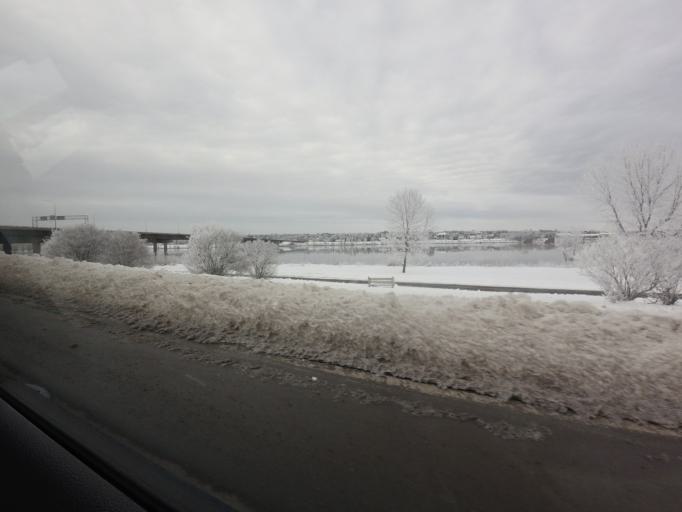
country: CA
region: New Brunswick
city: Fredericton
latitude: 45.9651
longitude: -66.6426
